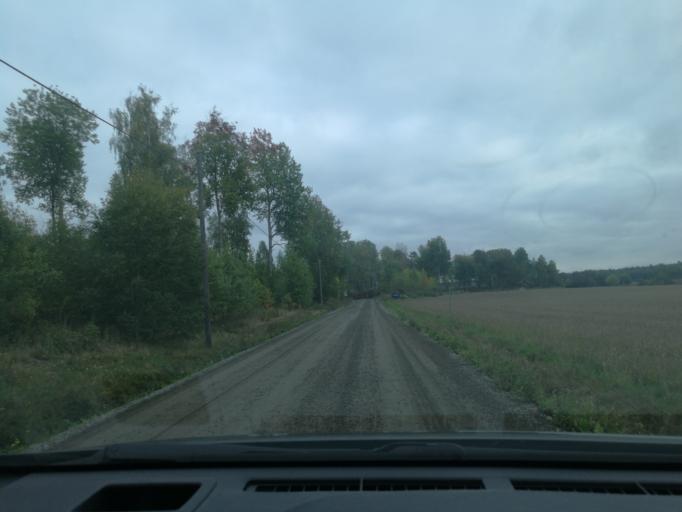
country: SE
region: Vaestmanland
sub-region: Vasteras
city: Tillberga
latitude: 59.7404
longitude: 16.6979
